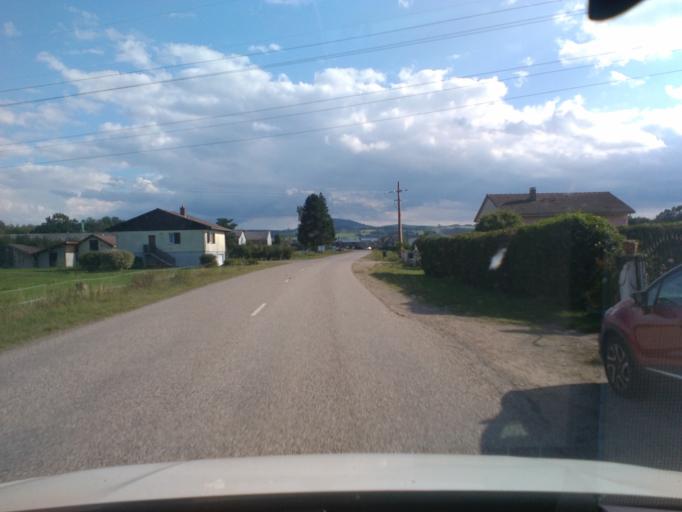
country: FR
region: Lorraine
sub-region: Departement des Vosges
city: Corcieux
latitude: 48.1885
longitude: 6.8821
